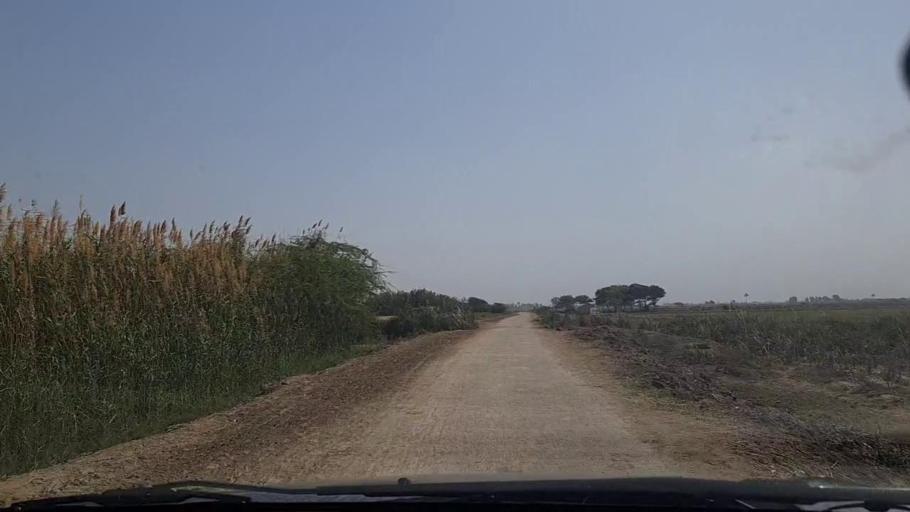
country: PK
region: Sindh
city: Keti Bandar
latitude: 24.2717
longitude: 67.6721
